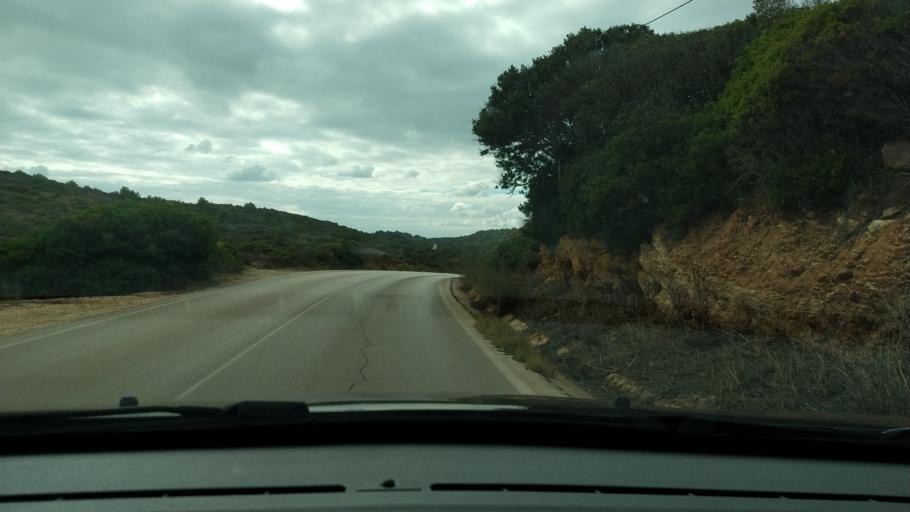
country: PT
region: Faro
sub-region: Lagos
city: Lagos
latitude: 37.0705
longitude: -8.7861
